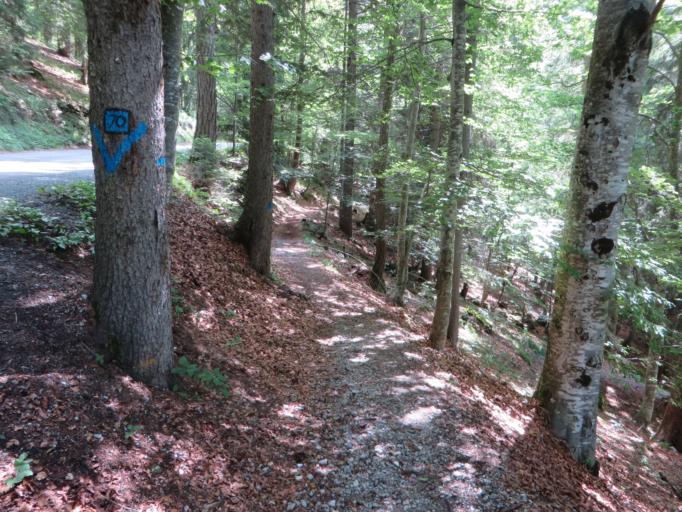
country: IT
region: Trentino-Alto Adige
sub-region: Provincia di Trento
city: Carisolo
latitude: 46.2096
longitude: 10.8393
